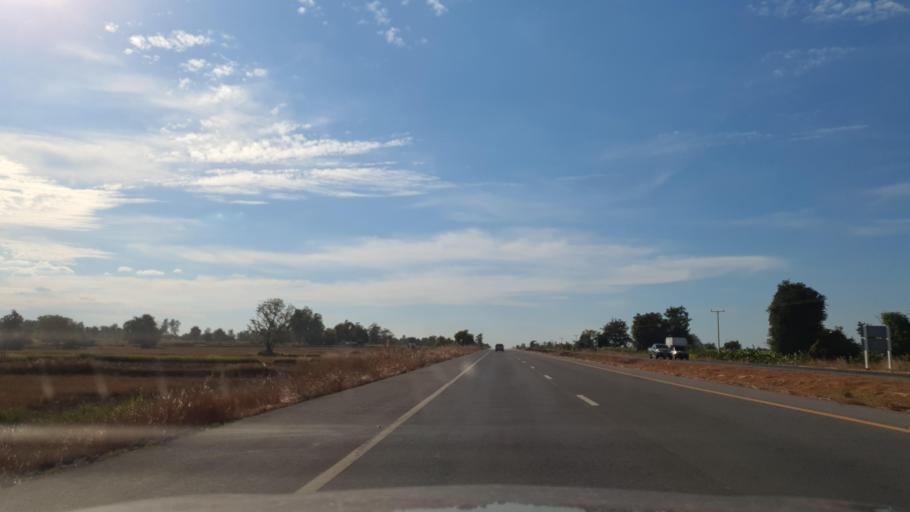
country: TH
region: Kalasin
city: Don Chan
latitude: 16.4108
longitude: 103.7311
